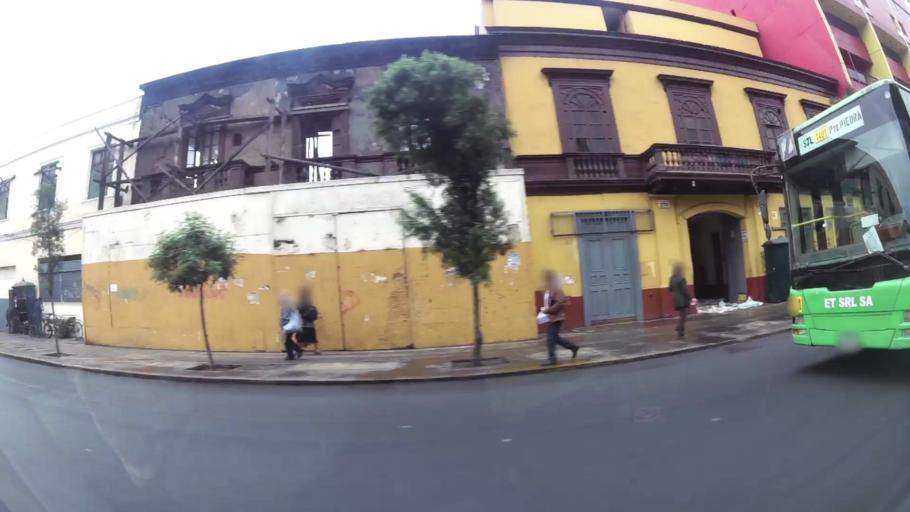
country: PE
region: Lima
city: Lima
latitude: -12.0483
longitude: -77.0271
